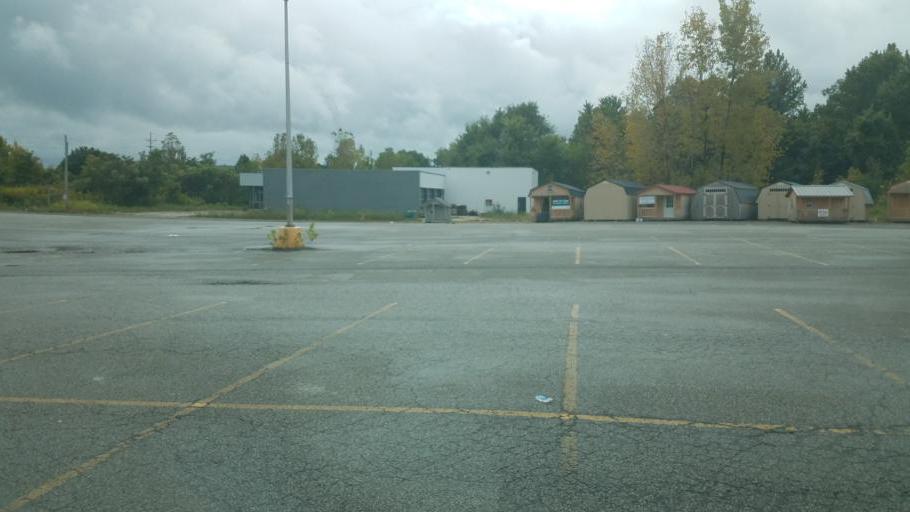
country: US
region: Ohio
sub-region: Scioto County
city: Wheelersburg
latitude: 38.7126
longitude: -82.8570
